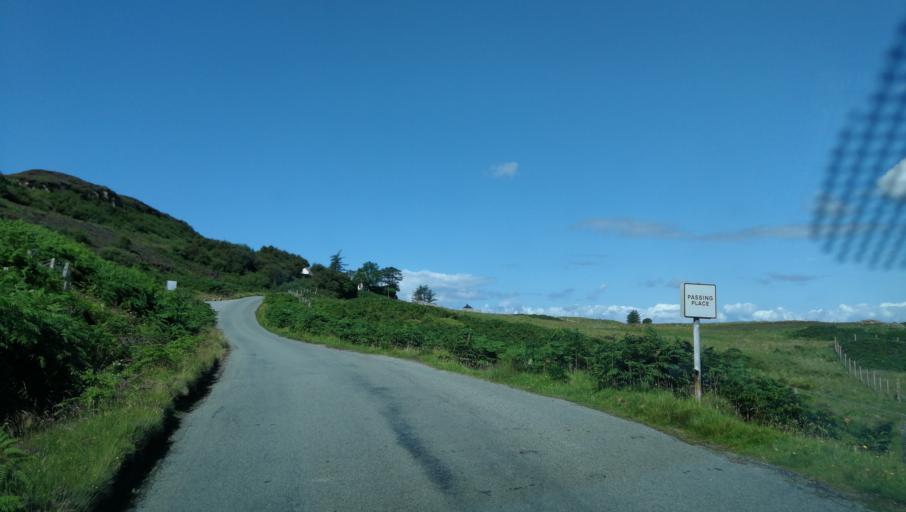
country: GB
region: Scotland
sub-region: Highland
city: Isle of Skye
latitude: 57.4498
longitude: -6.6533
